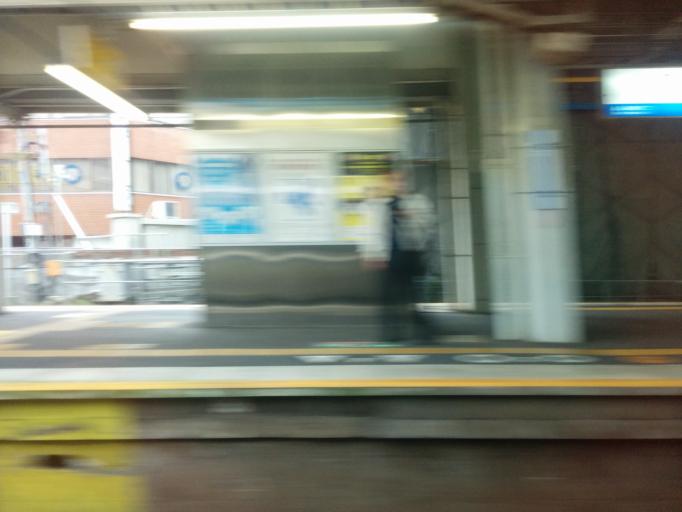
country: JP
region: Shiga Prefecture
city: Kusatsu
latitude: 34.9870
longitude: 135.9256
